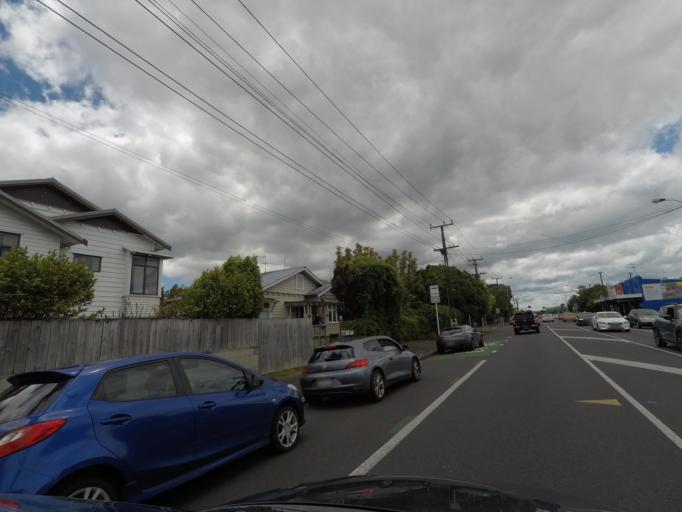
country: NZ
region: Auckland
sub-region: Auckland
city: Auckland
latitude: -36.8871
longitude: 174.7378
